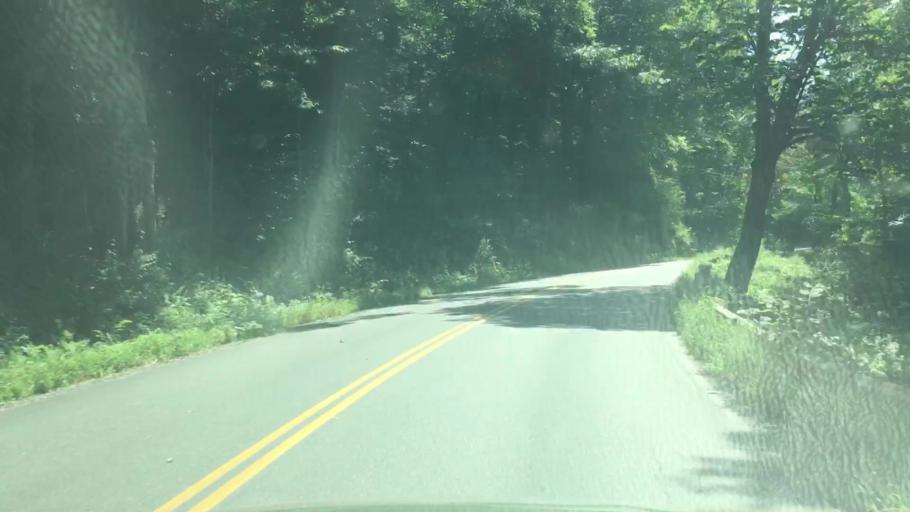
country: US
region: Vermont
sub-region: Windham County
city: West Brattleboro
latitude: 42.8039
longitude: -72.6047
